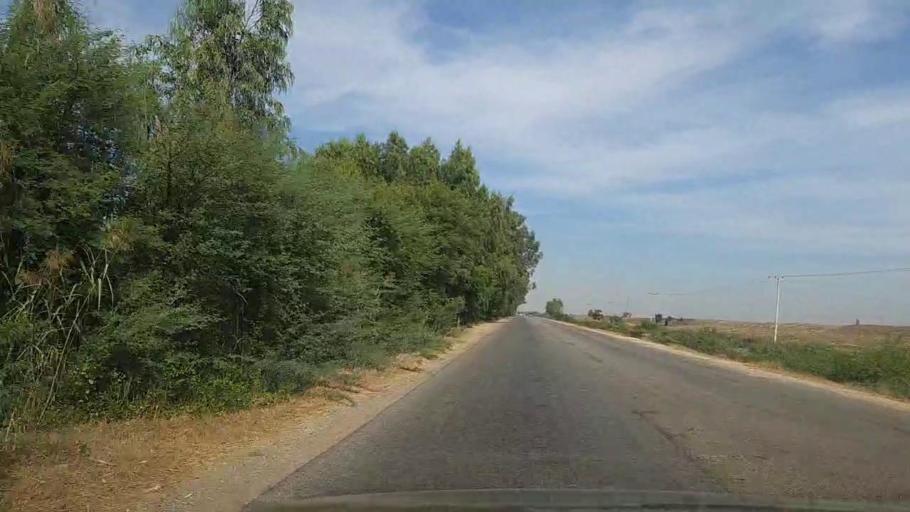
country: PK
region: Sindh
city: Daro Mehar
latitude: 24.9564
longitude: 68.1155
